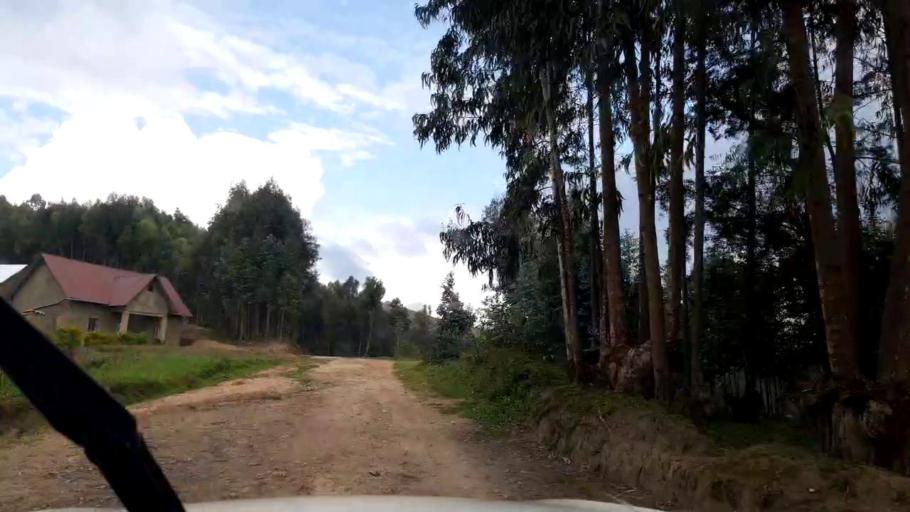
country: RW
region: Southern Province
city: Gitarama
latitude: -1.8672
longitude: 29.5687
